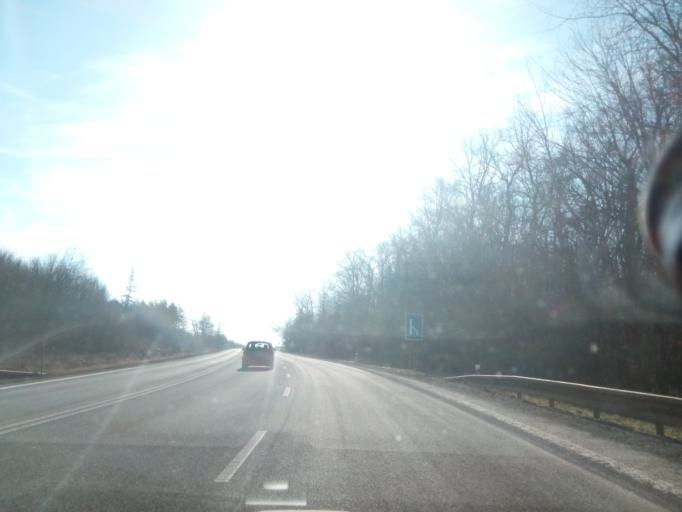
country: SK
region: Kosicky
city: Secovce
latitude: 48.7420
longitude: 21.5320
